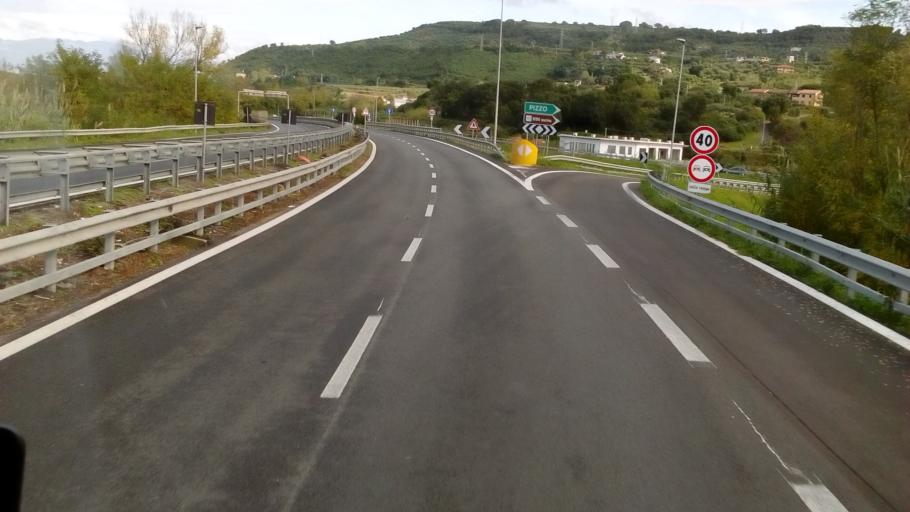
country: IT
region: Calabria
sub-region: Provincia di Vibo-Valentia
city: Pizzo
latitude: 38.7718
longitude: 16.2133
